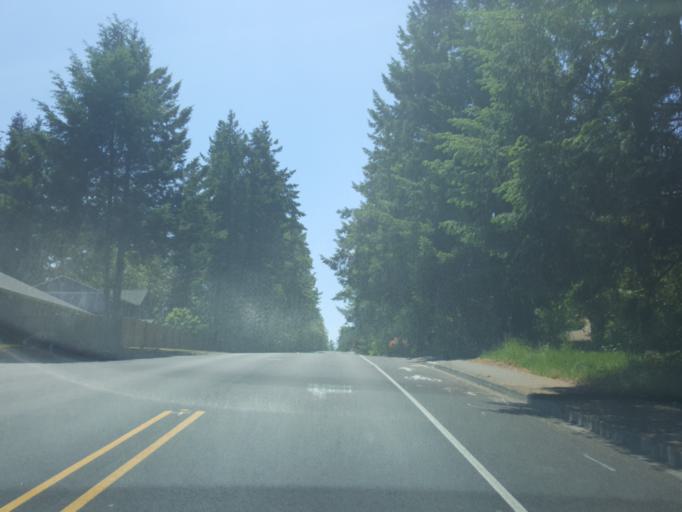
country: US
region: Washington
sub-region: Pierce County
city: Steilacoom
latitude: 47.1697
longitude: -122.5851
